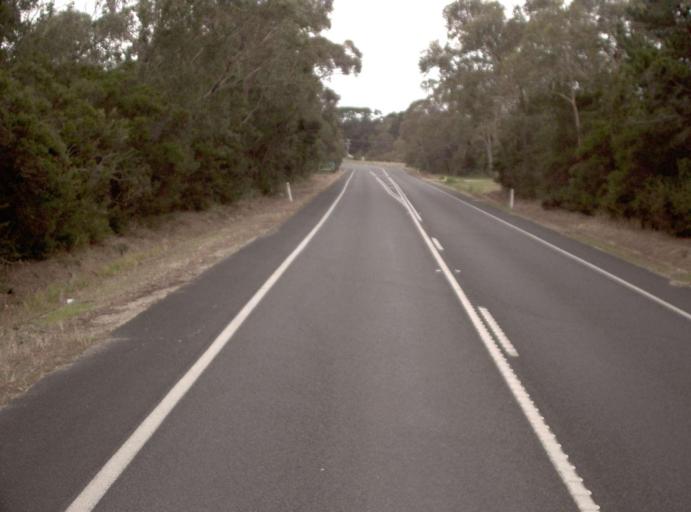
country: AU
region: Victoria
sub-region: Wellington
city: Sale
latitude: -38.1769
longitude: 147.0863
